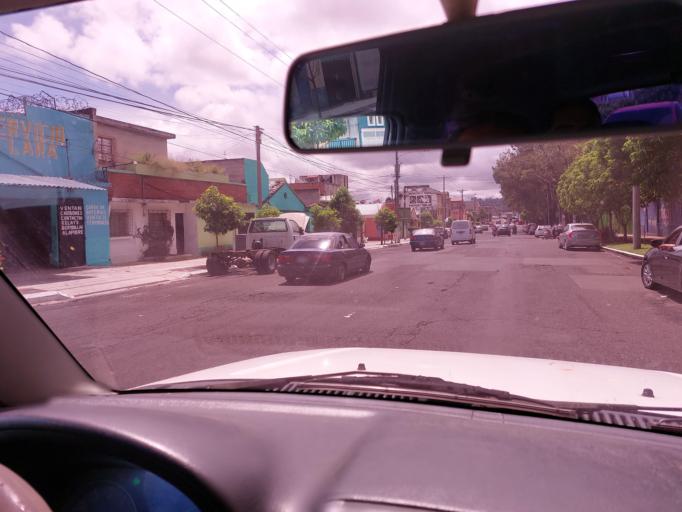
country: GT
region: Guatemala
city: Guatemala City
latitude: 14.6248
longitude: -90.5020
